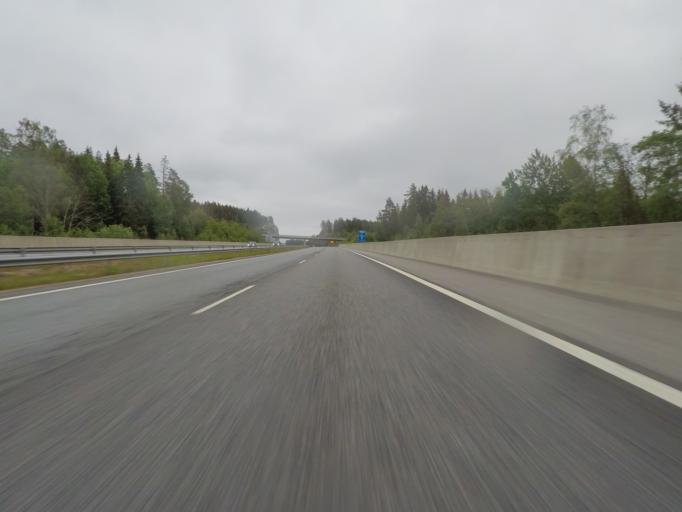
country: FI
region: Varsinais-Suomi
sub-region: Salo
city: Suomusjaervi
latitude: 60.3853
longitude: 23.5979
